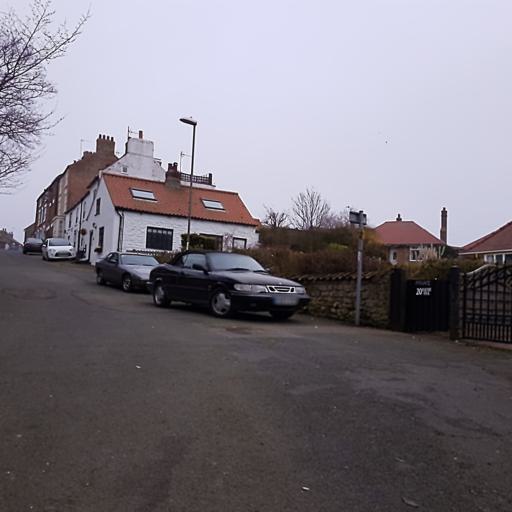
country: GB
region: England
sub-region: North Yorkshire
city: Filey
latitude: 54.2132
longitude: -0.2887
